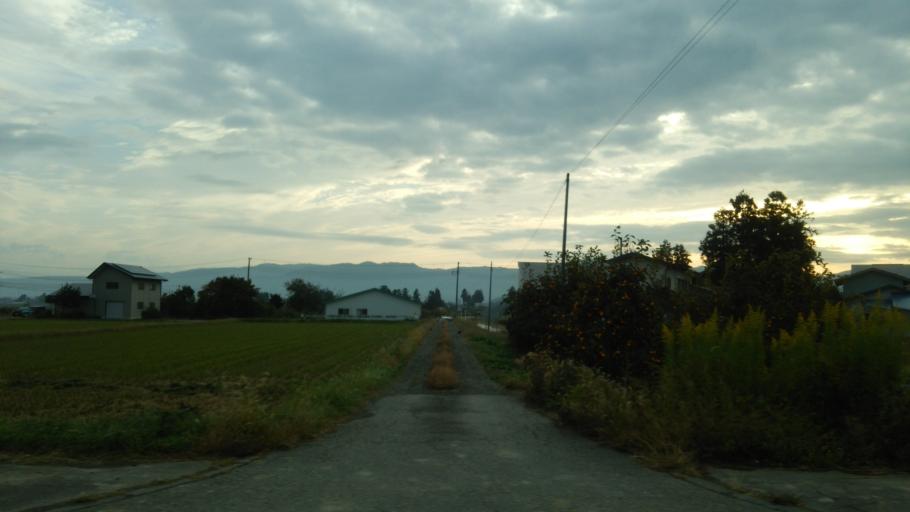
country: JP
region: Fukushima
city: Kitakata
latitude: 37.4552
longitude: 139.8555
